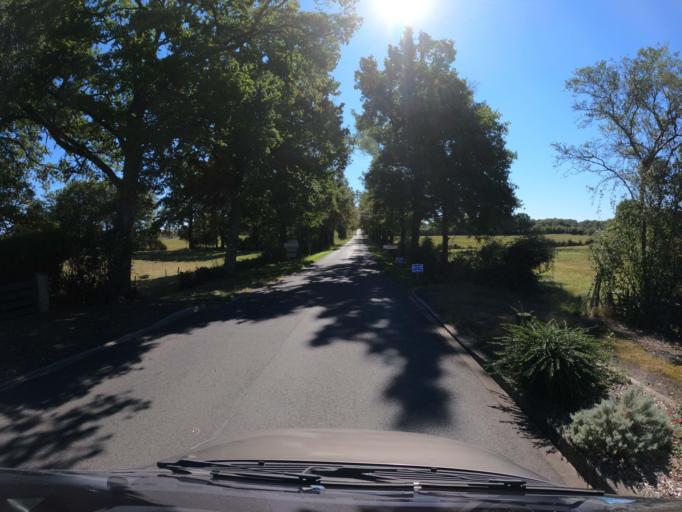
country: FR
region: Poitou-Charentes
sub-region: Departement de la Vienne
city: Lathus-Saint-Remy
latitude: 46.3295
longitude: 0.9642
